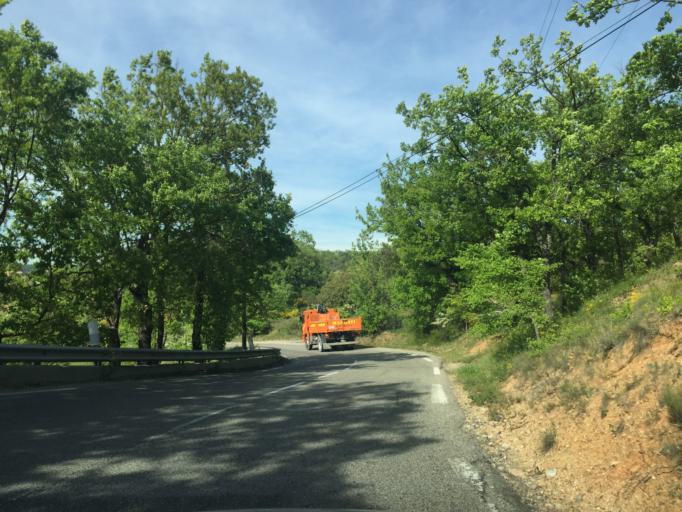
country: FR
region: Provence-Alpes-Cote d'Azur
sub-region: Departement du Var
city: Vinon-sur-Verdon
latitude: 43.7194
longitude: 5.8120
